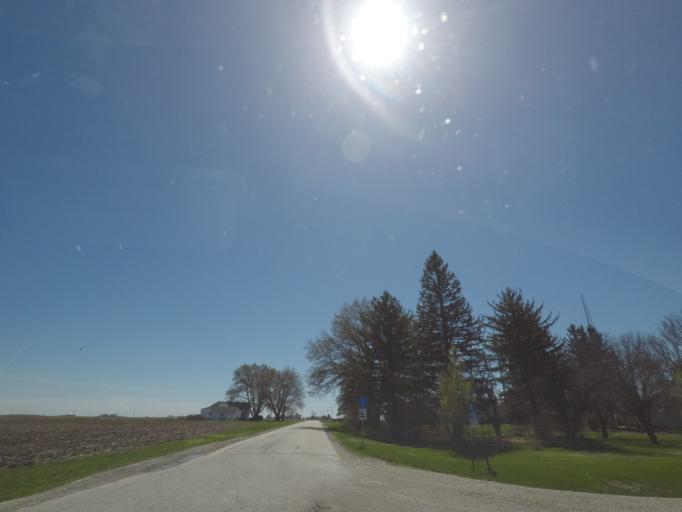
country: US
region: Illinois
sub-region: Logan County
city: Mount Pulaski
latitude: 40.0529
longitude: -89.1824
